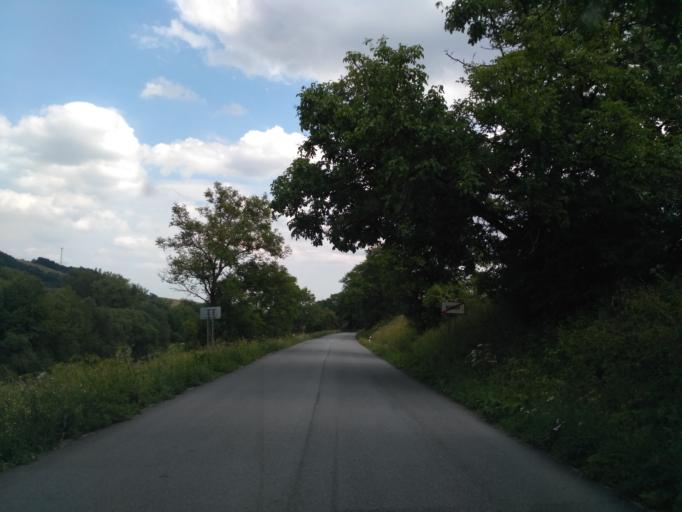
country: SK
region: Kosicky
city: Gelnica
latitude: 48.9242
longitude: 21.0591
